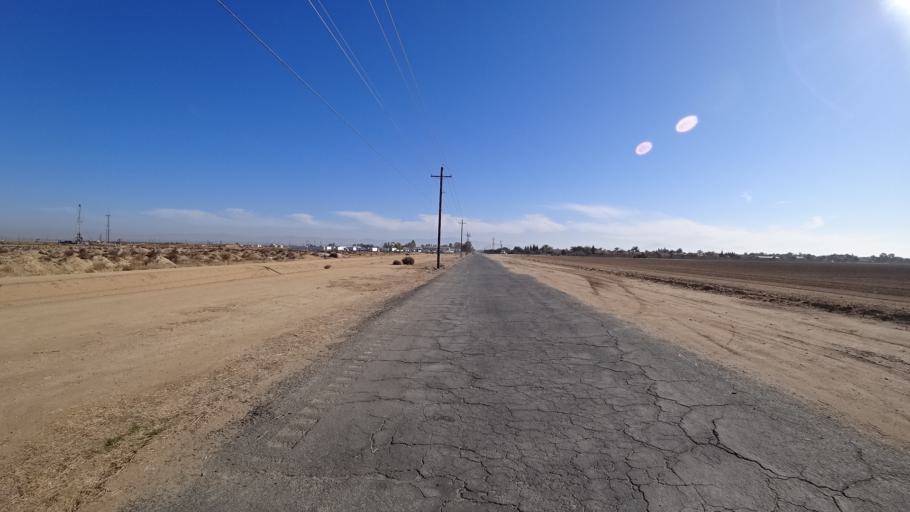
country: US
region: California
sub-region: Kern County
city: Rosedale
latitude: 35.4270
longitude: -119.1488
